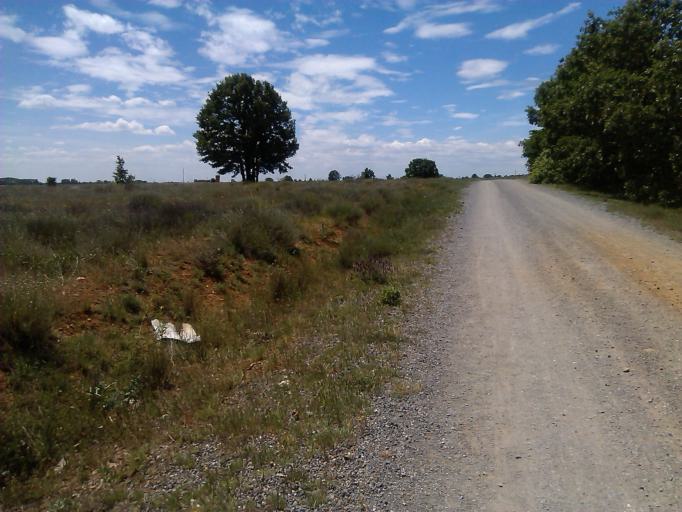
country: ES
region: Castille and Leon
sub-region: Provincia de Leon
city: Chozas de Abajo
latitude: 42.5211
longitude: -5.6802
